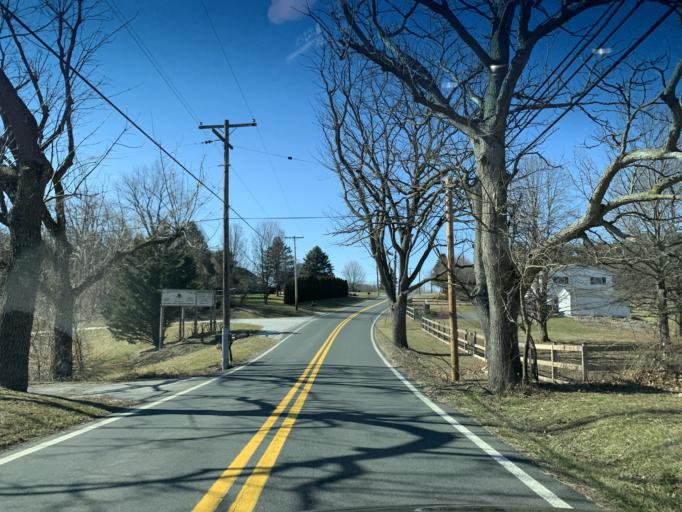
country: US
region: Maryland
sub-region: Carroll County
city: Hampstead
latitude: 39.5864
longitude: -76.9198
